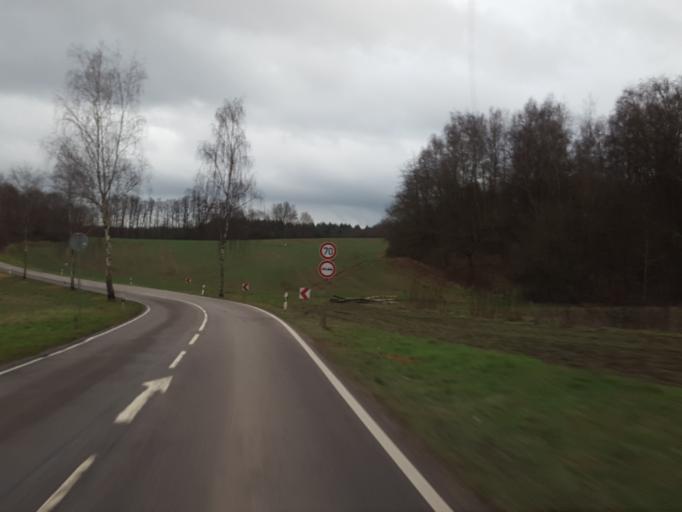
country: DE
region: Saarland
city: Beckingen
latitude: 49.4285
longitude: 6.7411
